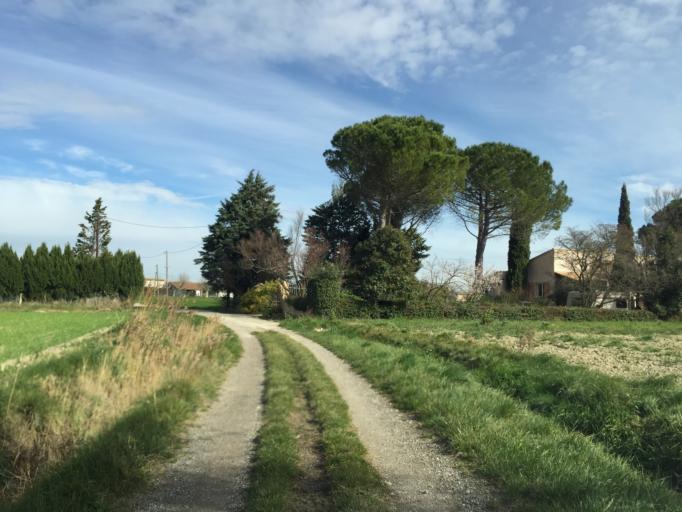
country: FR
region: Provence-Alpes-Cote d'Azur
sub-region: Departement du Vaucluse
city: Caderousse
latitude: 44.1239
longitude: 4.7515
